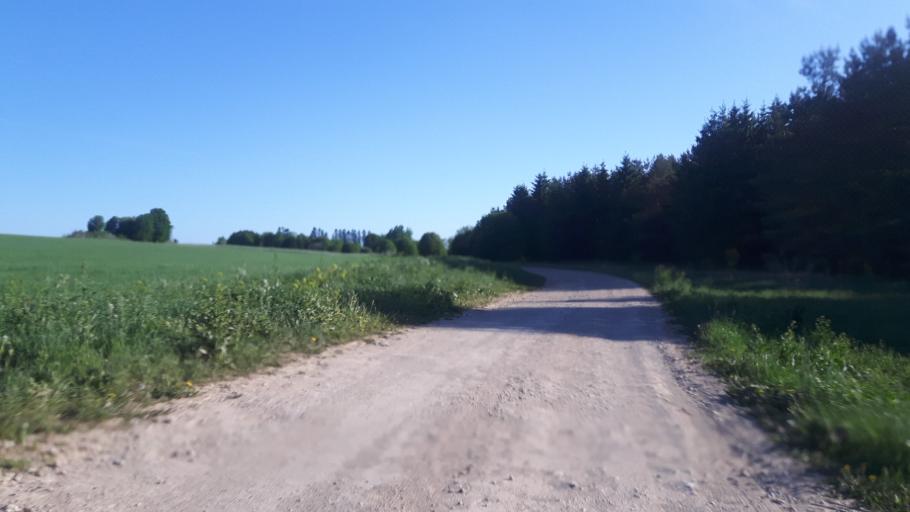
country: EE
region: Ida-Virumaa
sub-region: Puessi linn
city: Pussi
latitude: 59.4231
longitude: 27.0648
